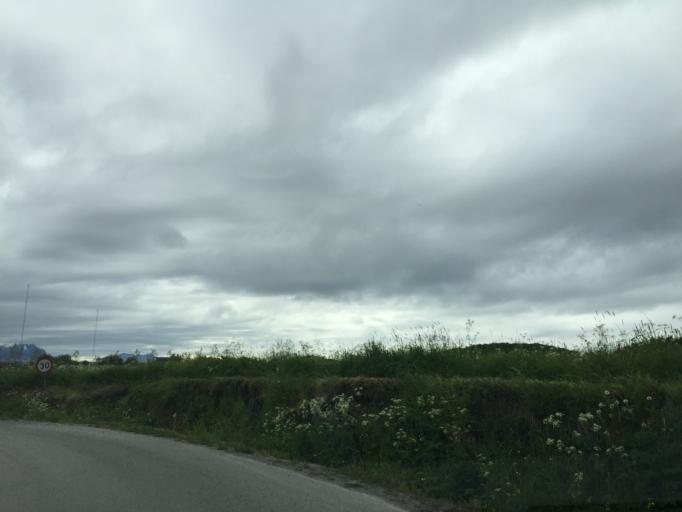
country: NO
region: Nordland
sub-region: Bodo
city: Bodo
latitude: 67.2712
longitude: 14.4270
